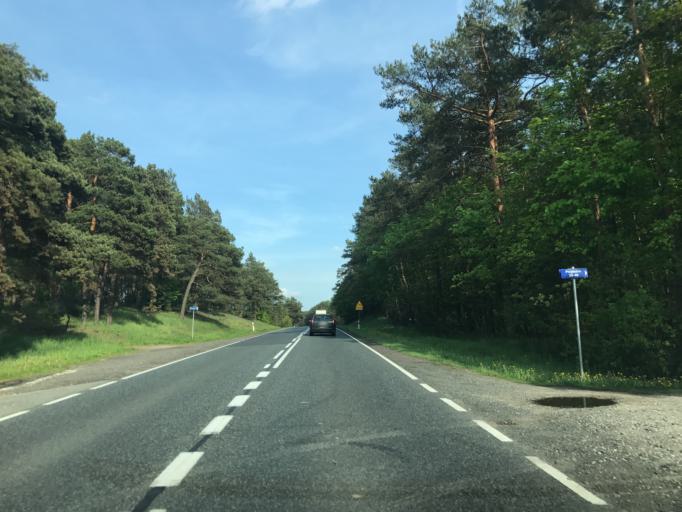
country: PL
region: Kujawsko-Pomorskie
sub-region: Powiat torunski
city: Zlawies Wielka
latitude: 53.0515
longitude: 18.3333
